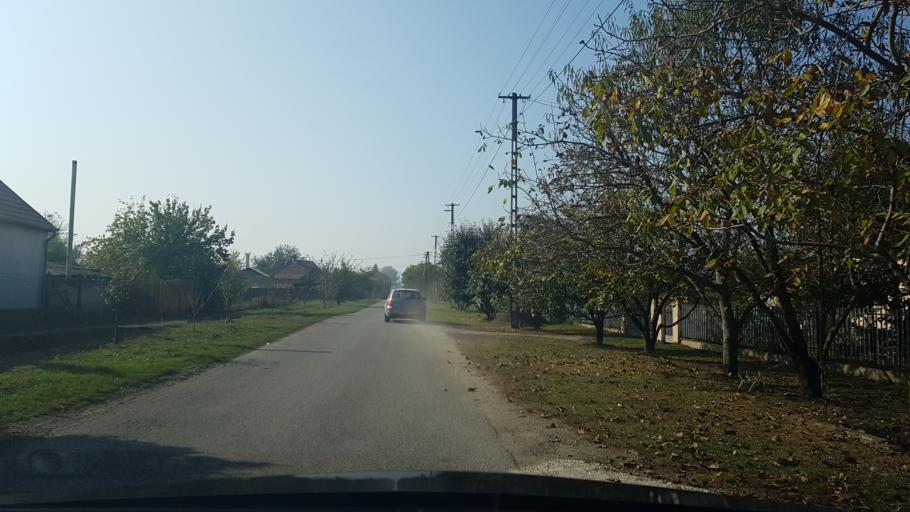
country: HU
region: Fejer
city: Pusztaszabolcs
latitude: 47.1445
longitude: 18.7574
